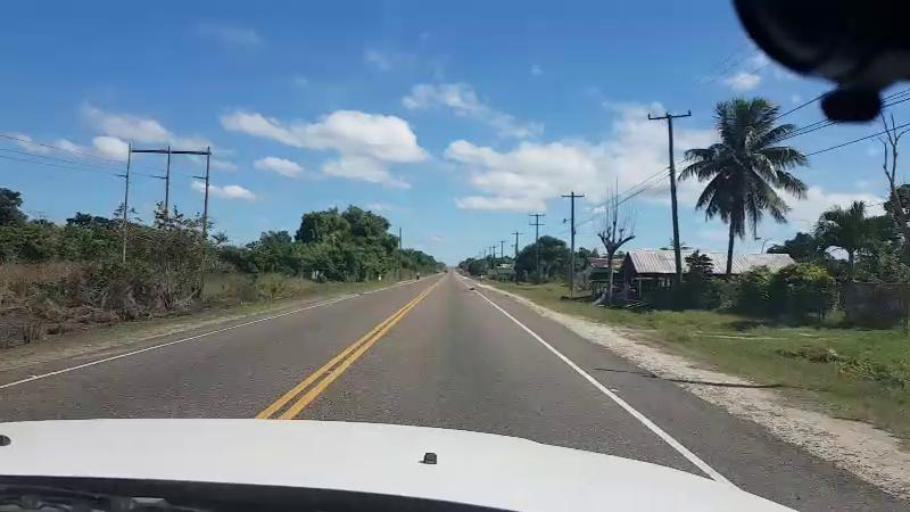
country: BZ
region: Cayo
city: Belmopan
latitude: 17.2769
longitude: -88.7156
